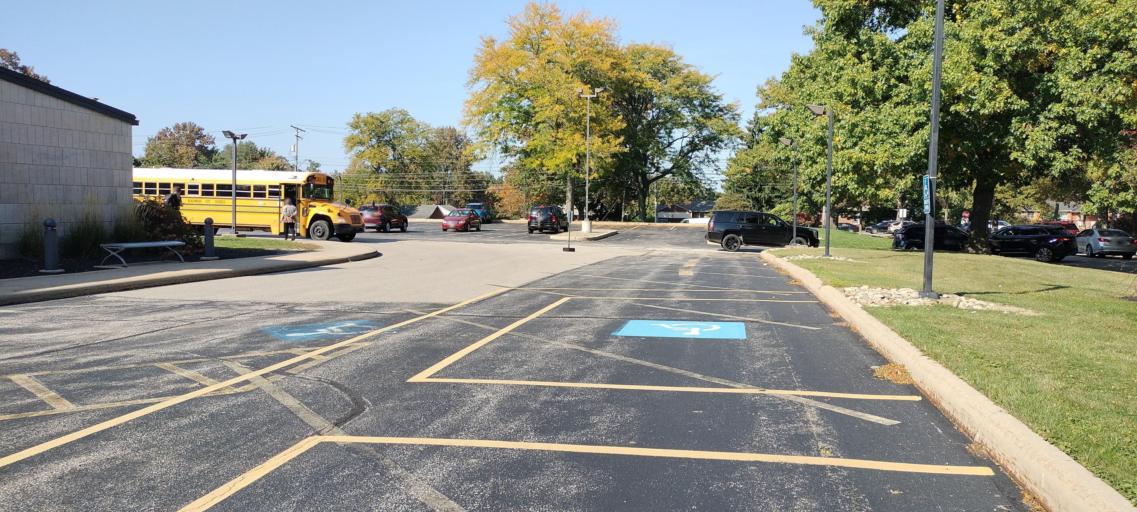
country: US
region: Ohio
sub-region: Cuyahoga County
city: Mayfield Heights
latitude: 41.5380
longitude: -81.4592
